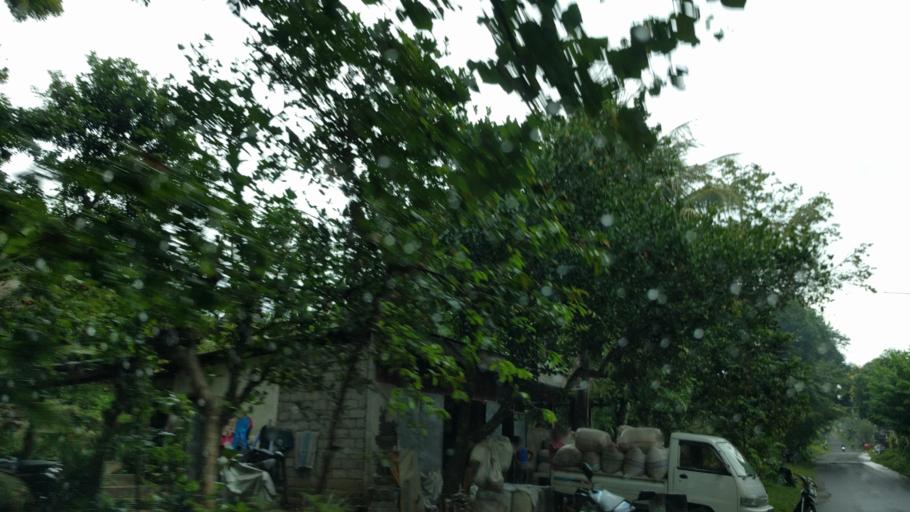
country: ID
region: Bali
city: Banjar Triwangsakeliki
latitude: -8.4560
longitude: 115.2603
